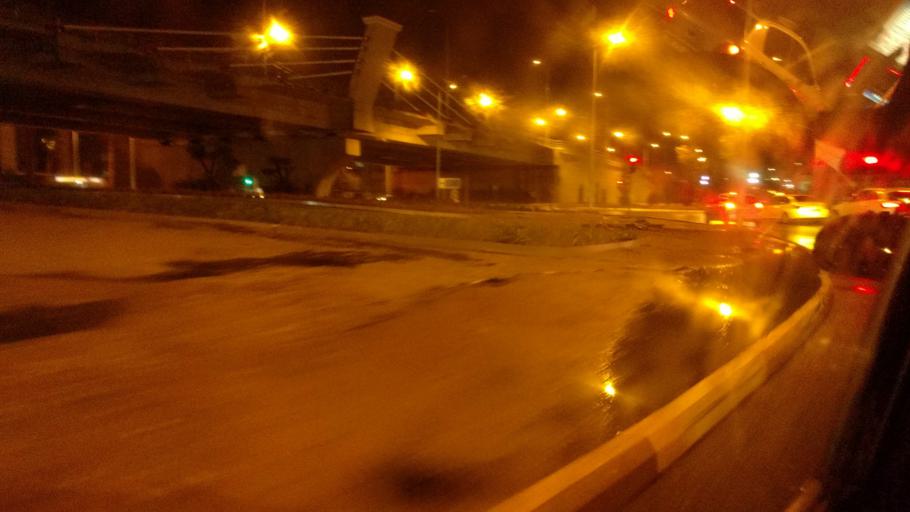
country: TR
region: Antalya
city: Antalya
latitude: 36.9058
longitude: 30.6824
